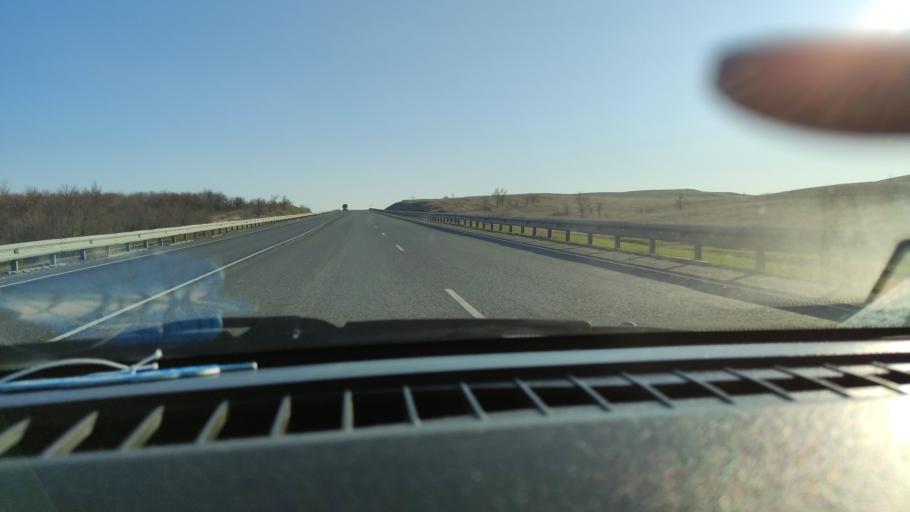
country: RU
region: Saratov
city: Alekseyevka
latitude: 52.2189
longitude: 47.8939
